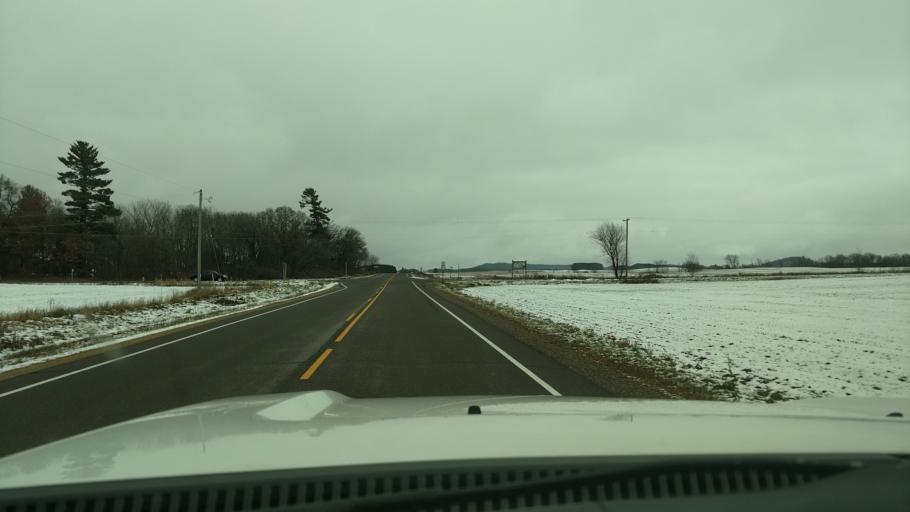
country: US
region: Wisconsin
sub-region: Dunn County
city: Colfax
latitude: 45.1427
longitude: -91.6887
